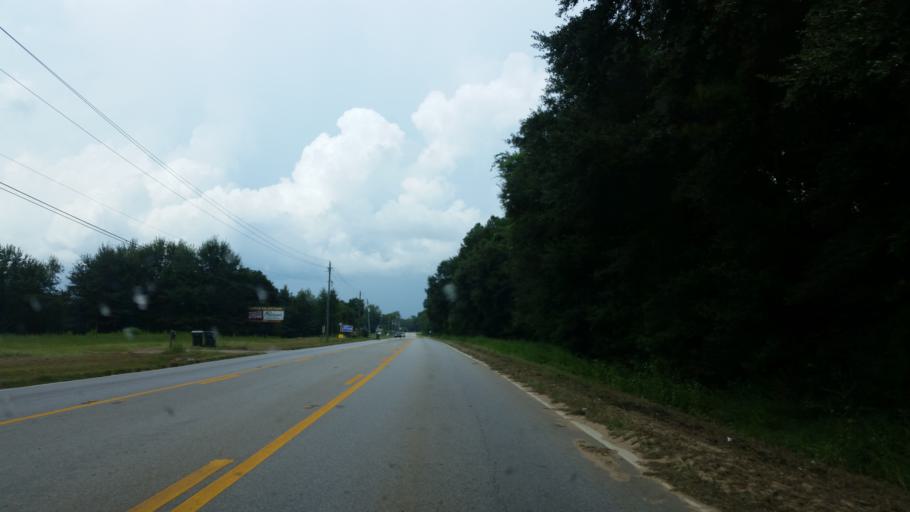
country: US
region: Florida
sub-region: Santa Rosa County
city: Pace
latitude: 30.6304
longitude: -87.1816
